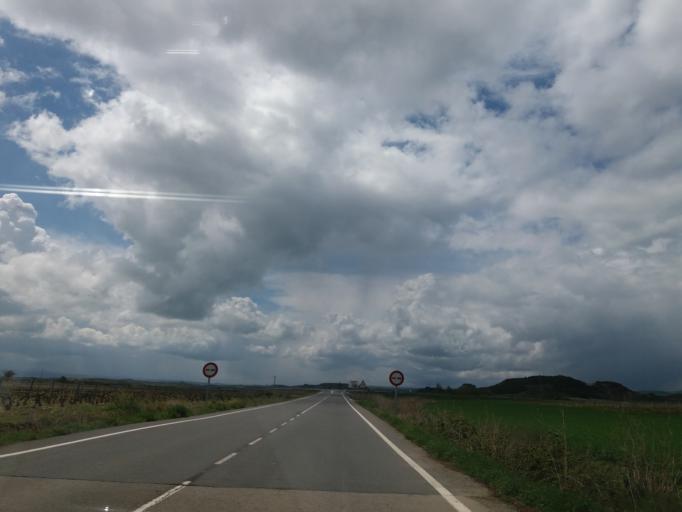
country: ES
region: La Rioja
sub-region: Provincia de La Rioja
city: Sajazarra
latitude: 42.5714
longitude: -2.9545
